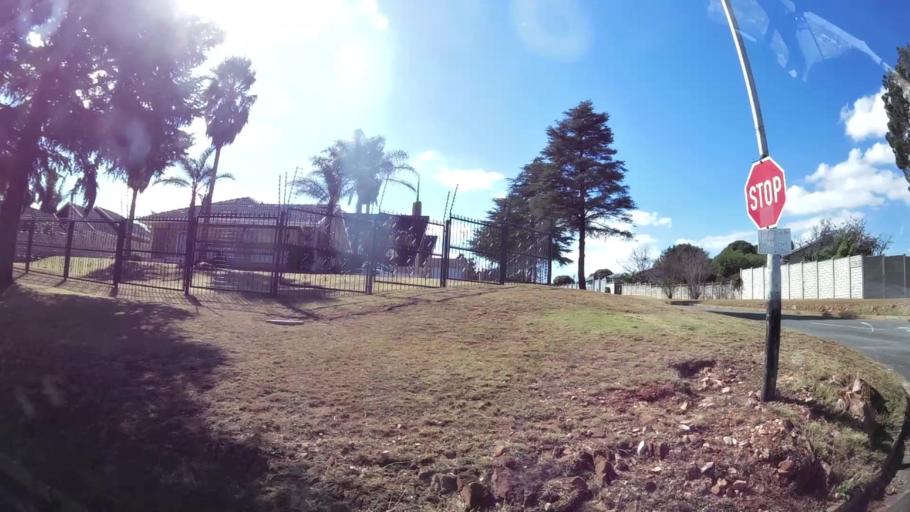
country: ZA
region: Gauteng
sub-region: West Rand District Municipality
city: Krugersdorp
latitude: -26.1050
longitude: 27.7968
